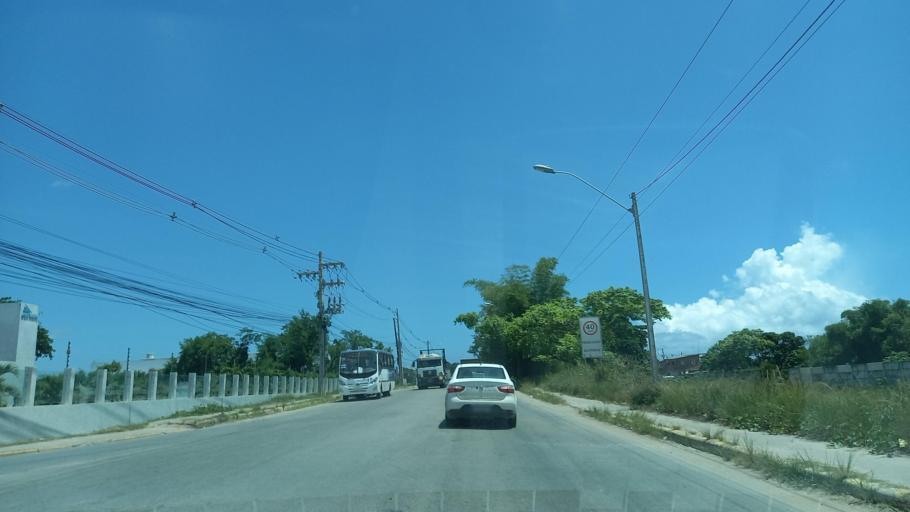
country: BR
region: Pernambuco
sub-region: Jaboatao Dos Guararapes
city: Jaboatao
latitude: -8.1547
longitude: -34.9607
